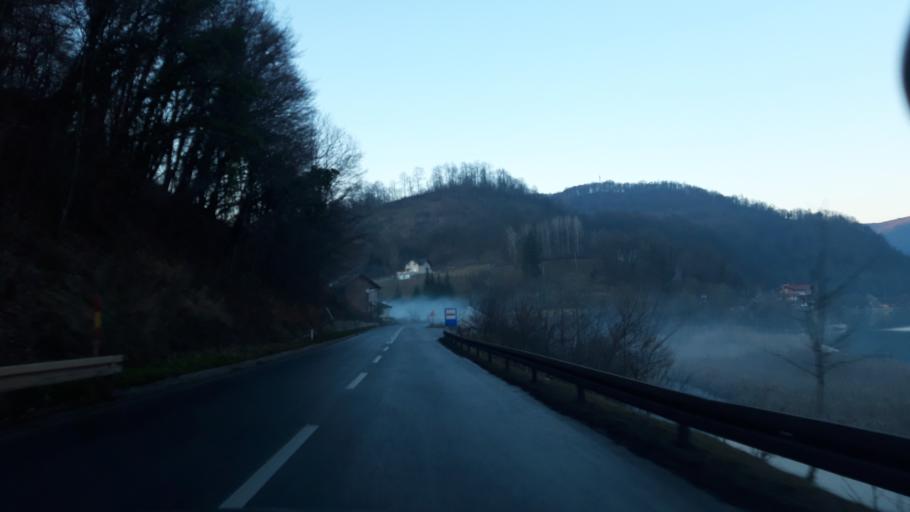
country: RS
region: Central Serbia
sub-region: Macvanski Okrug
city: Mali Zvornik
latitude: 44.3247
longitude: 19.1270
